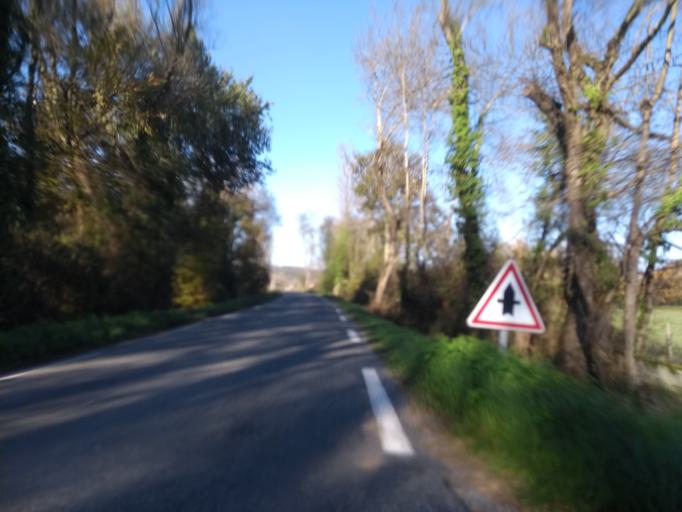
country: FR
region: Aquitaine
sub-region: Departement de la Gironde
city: Ayguemorte-les-Graves
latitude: 44.7189
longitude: -0.4693
